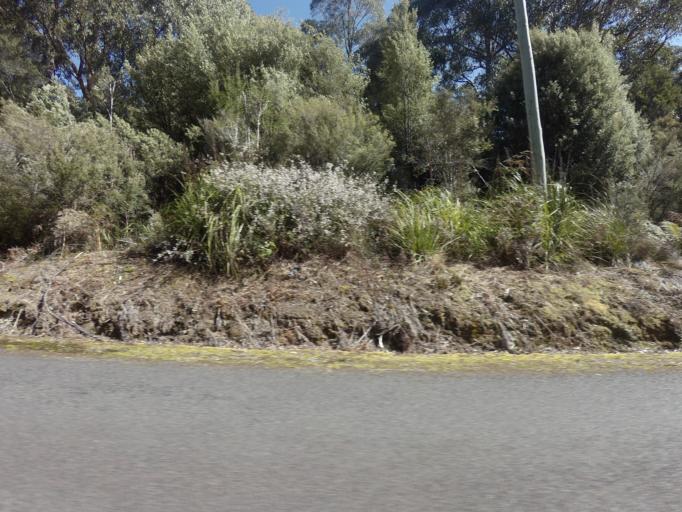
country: AU
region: Tasmania
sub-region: Derwent Valley
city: New Norfolk
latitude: -42.7644
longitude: 146.5501
